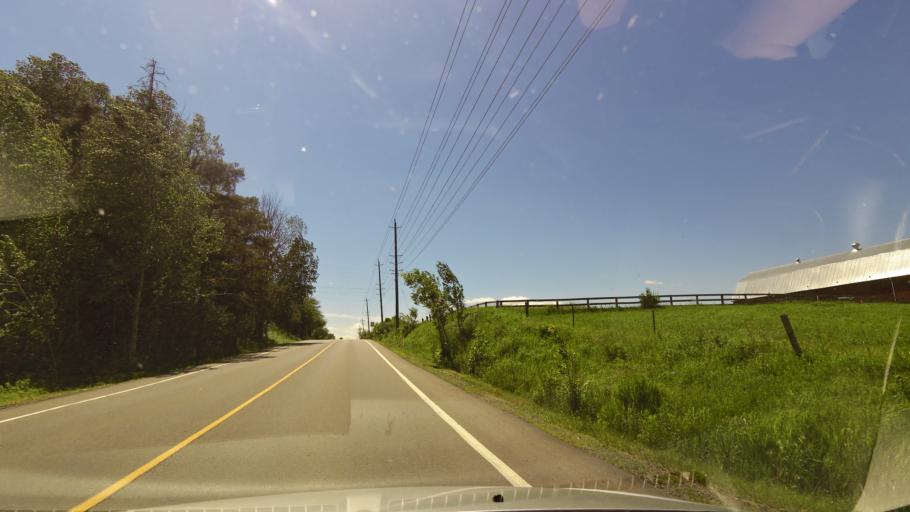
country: CA
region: Ontario
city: Newmarket
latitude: 43.9507
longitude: -79.5159
